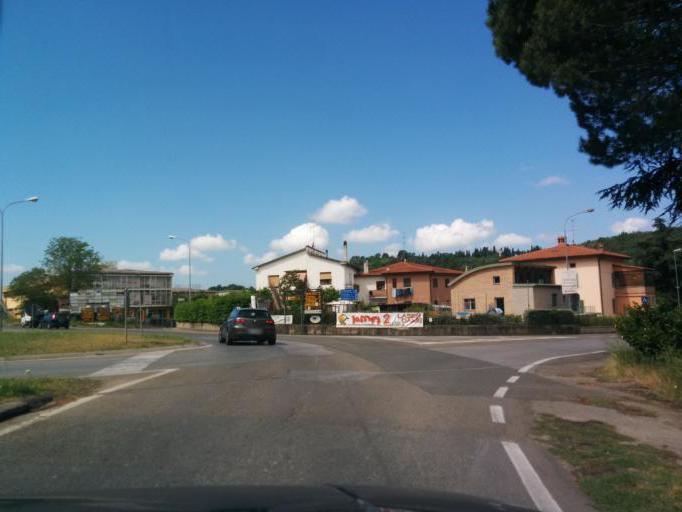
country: IT
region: Tuscany
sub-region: Provincia di Siena
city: Poggibonsi
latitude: 43.4699
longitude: 11.1274
